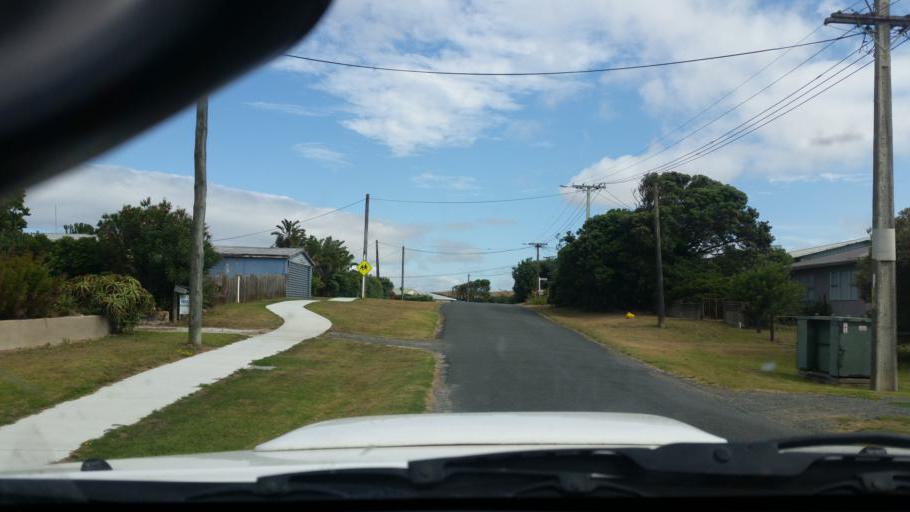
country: NZ
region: Northland
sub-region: Kaipara District
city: Dargaville
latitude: -35.9515
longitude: 173.7469
